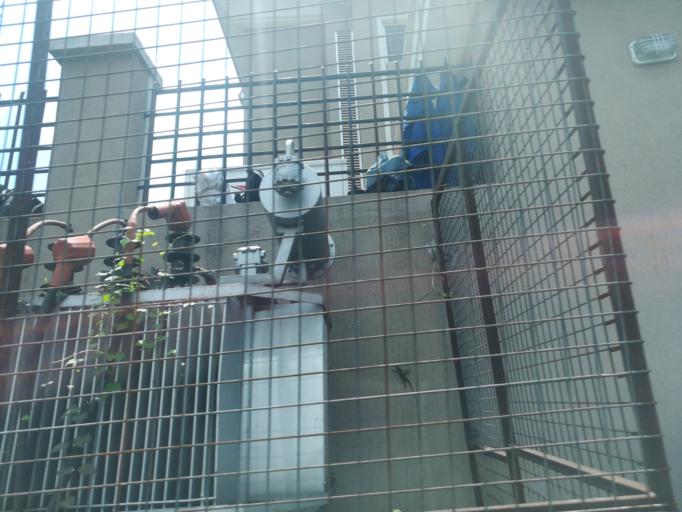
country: NG
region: Lagos
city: Somolu
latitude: 6.5446
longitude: 3.3662
